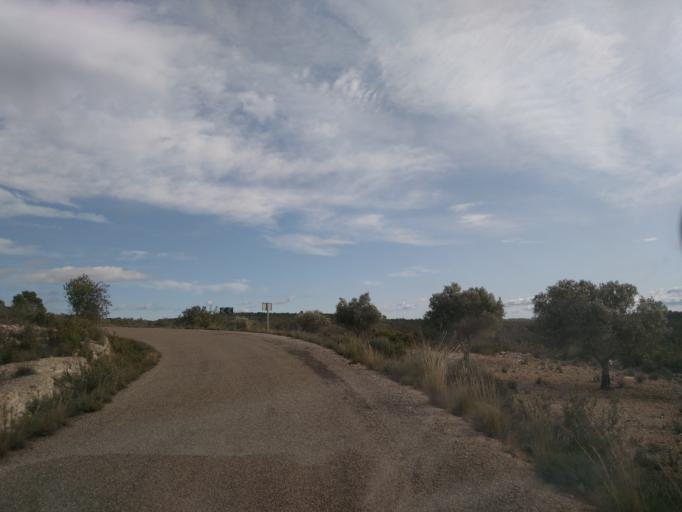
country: ES
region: Valencia
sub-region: Provincia de Valencia
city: Sumacarcer
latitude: 39.1460
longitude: -0.6456
